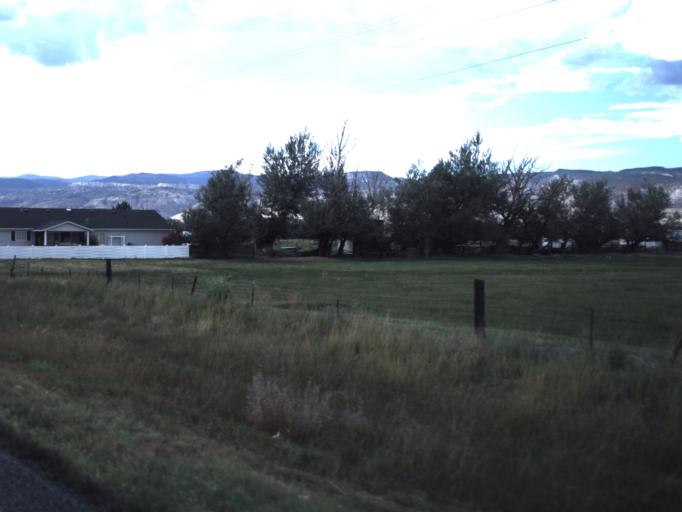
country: US
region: Utah
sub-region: Sevier County
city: Richfield
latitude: 38.7742
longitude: -112.0215
